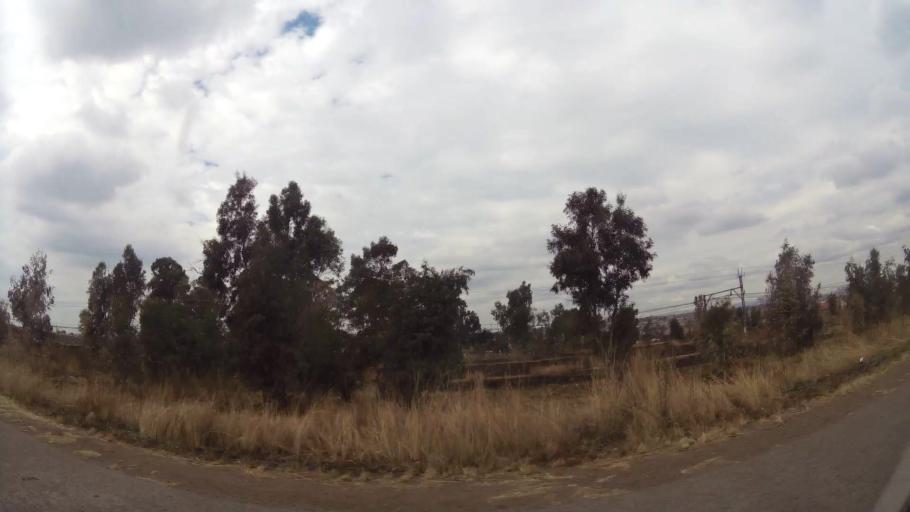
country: ZA
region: Gauteng
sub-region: Ekurhuleni Metropolitan Municipality
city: Germiston
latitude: -26.3666
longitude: 28.1151
